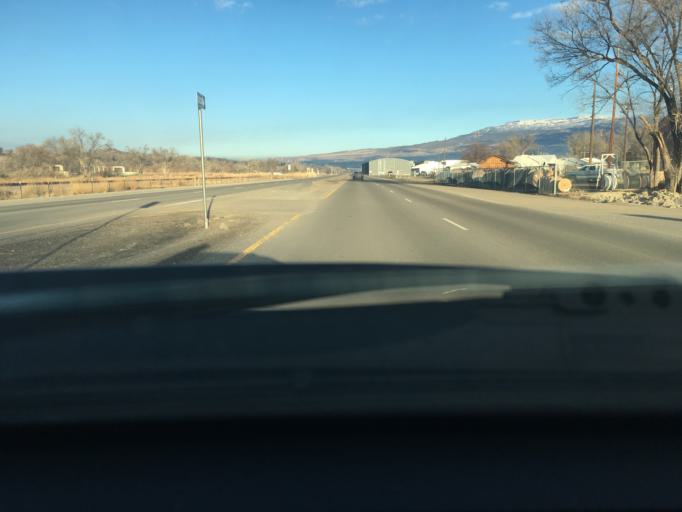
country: US
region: Colorado
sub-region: Delta County
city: Delta
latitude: 38.7313
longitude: -108.0716
